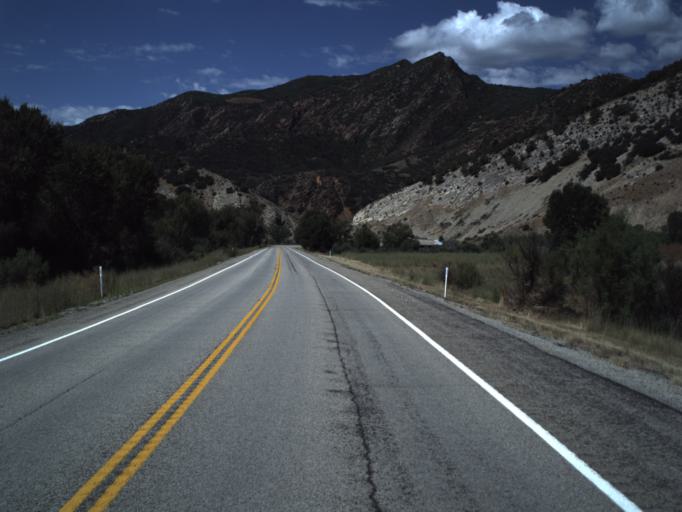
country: US
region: Utah
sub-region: Utah County
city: Mapleton
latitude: 39.9959
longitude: -111.4869
